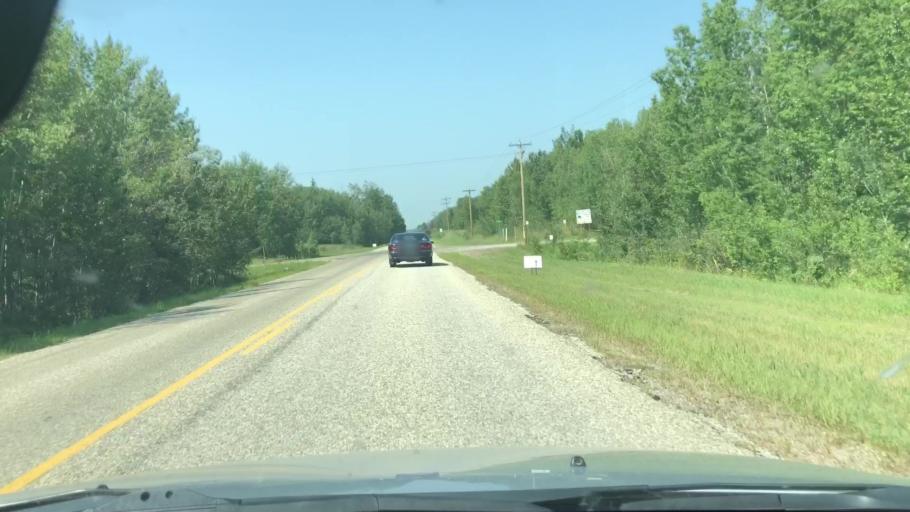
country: CA
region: Alberta
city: Devon
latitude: 53.4252
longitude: -113.7861
